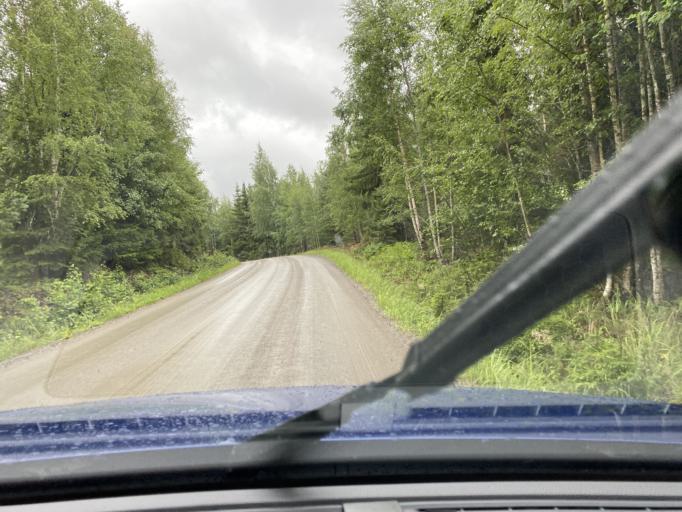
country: FI
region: Pirkanmaa
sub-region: Lounais-Pirkanmaa
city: Punkalaidun
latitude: 61.1468
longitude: 23.2644
